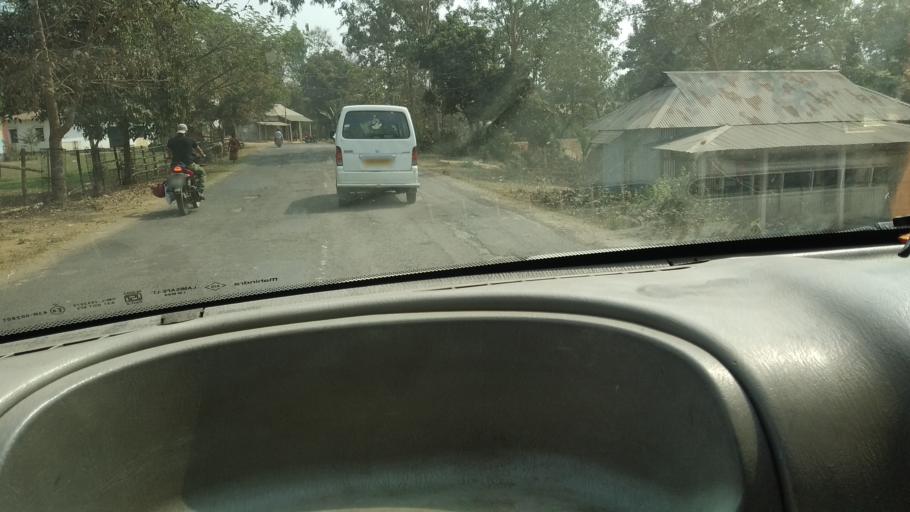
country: BD
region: Chittagong
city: Comilla
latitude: 23.5981
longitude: 91.1801
